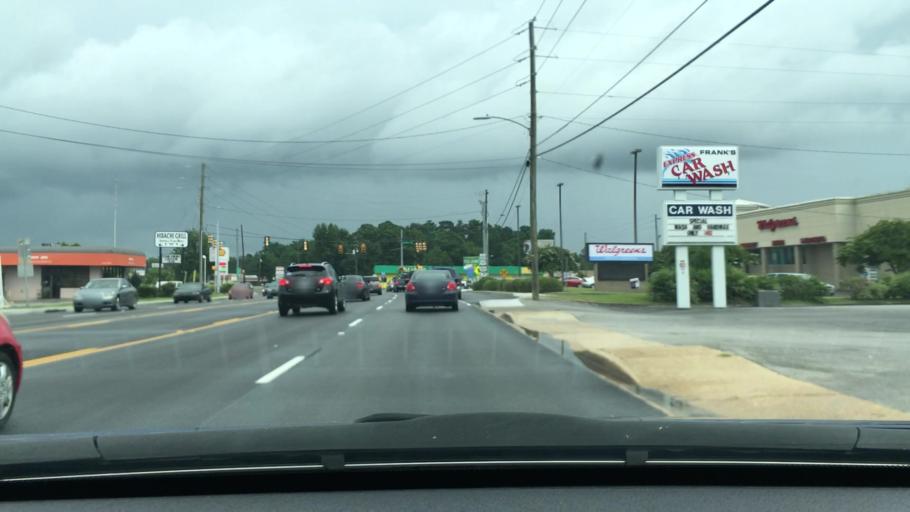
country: US
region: South Carolina
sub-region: Sumter County
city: Sumter
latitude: 33.9461
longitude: -80.3733
